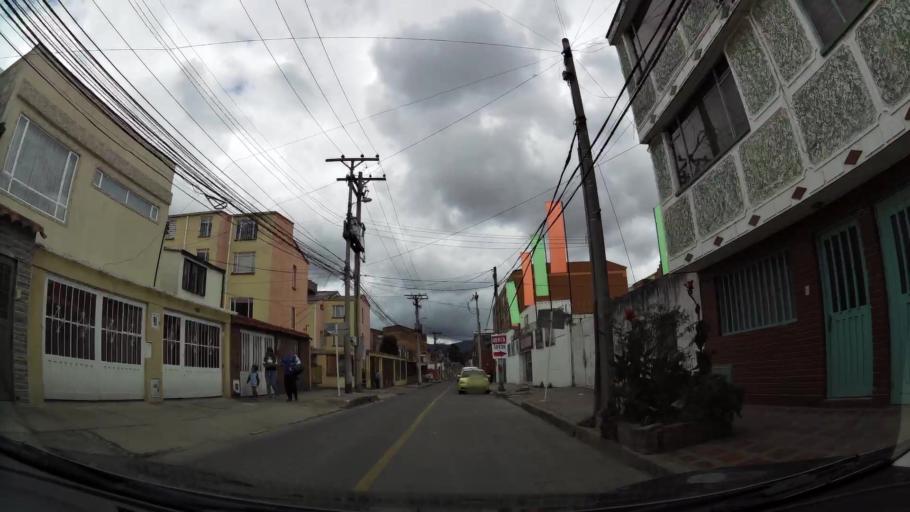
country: CO
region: Bogota D.C.
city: Barrio San Luis
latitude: 4.7035
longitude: -74.0918
